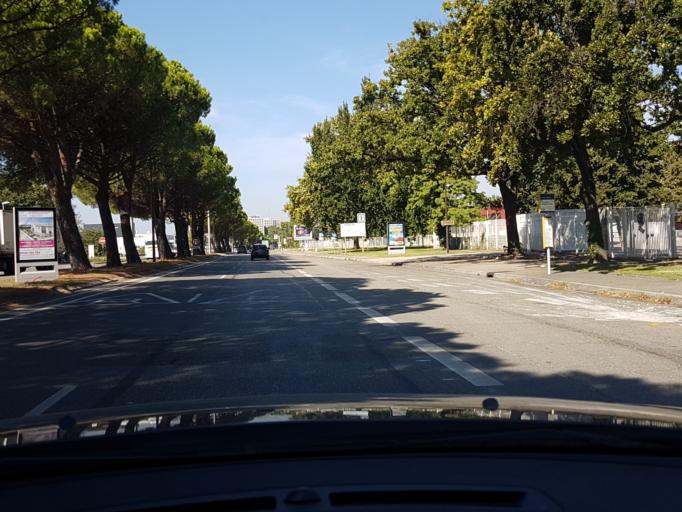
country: FR
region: Provence-Alpes-Cote d'Azur
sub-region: Departement du Vaucluse
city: Montfavet
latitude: 43.9272
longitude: 4.8443
